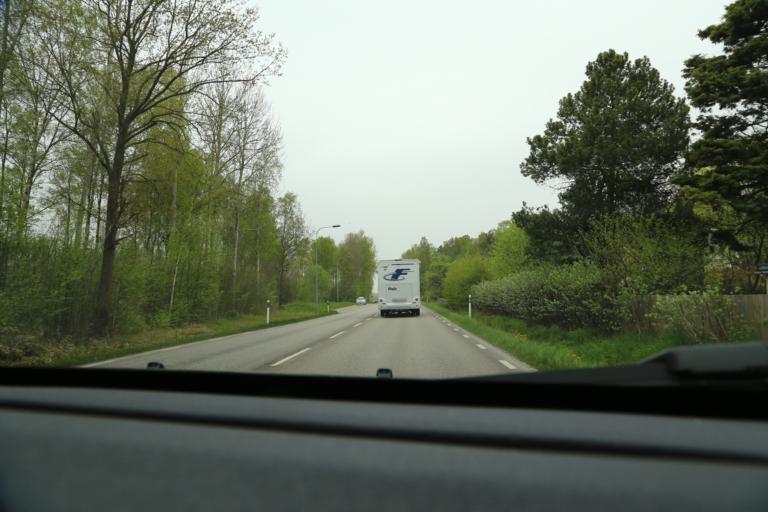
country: SE
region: Halland
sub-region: Varbergs Kommun
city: Varberg
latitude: 57.1756
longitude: 12.2283
